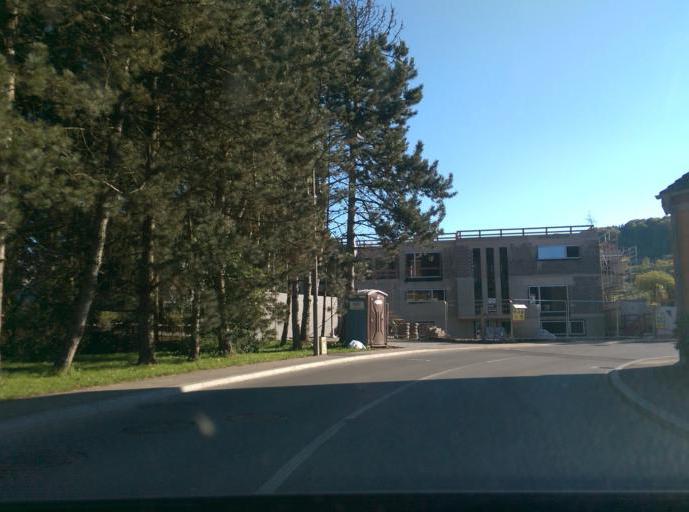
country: LU
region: Luxembourg
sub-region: Canton de Luxembourg
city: Niederanven
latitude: 49.6574
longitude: 6.2465
